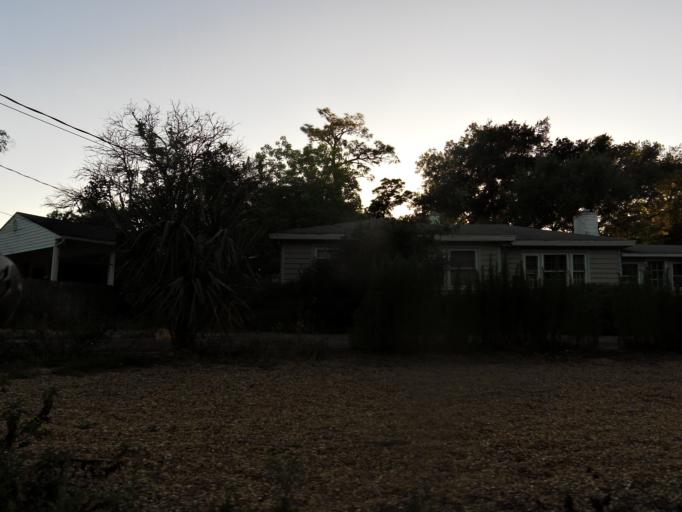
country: US
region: Florida
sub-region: Duval County
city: Jacksonville
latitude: 30.2626
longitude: -81.6372
